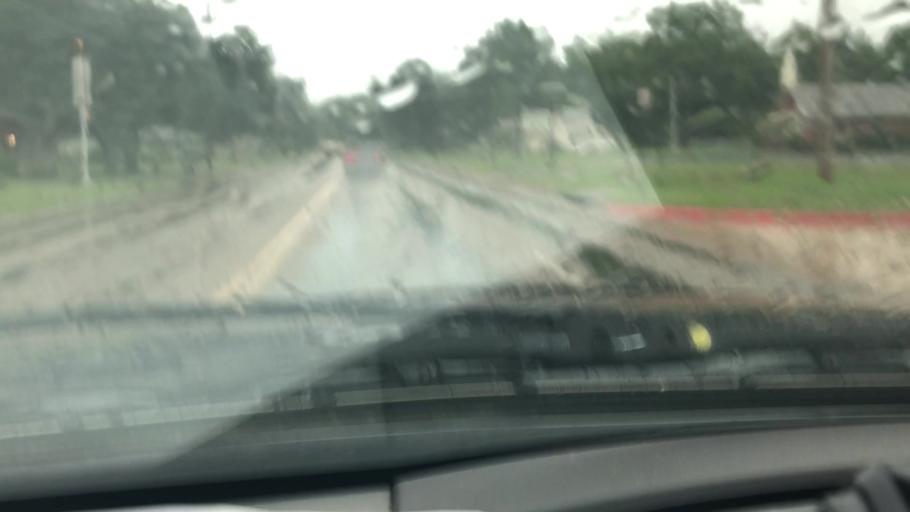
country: US
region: Texas
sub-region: Bowie County
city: Wake Village
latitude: 33.4361
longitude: -94.0866
